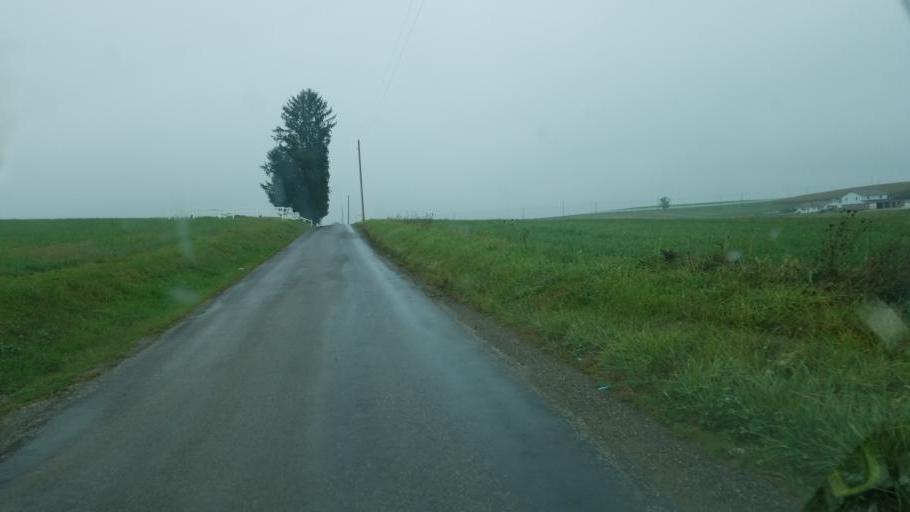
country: US
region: Ohio
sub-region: Tuscarawas County
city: Sugarcreek
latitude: 40.5673
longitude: -81.7525
